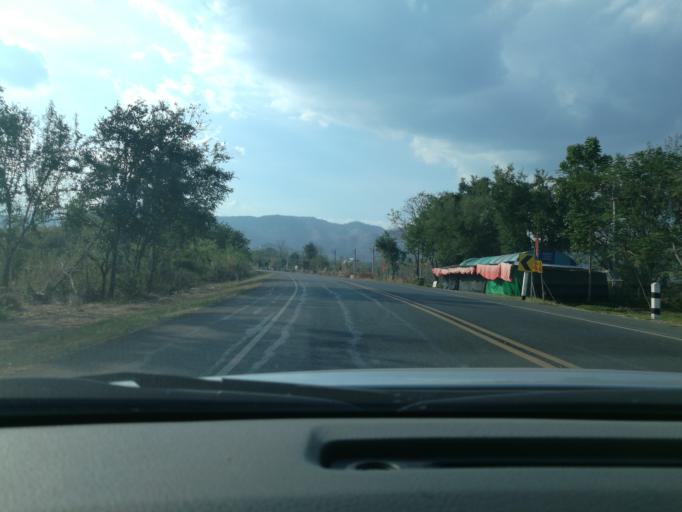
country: TH
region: Phetchabun
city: Phetchabun
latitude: 16.5488
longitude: 101.1383
